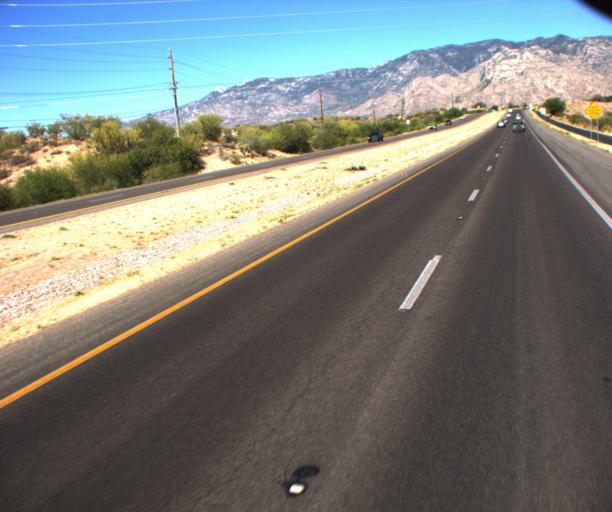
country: US
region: Arizona
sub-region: Pima County
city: Oro Valley
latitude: 32.4270
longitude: -110.9409
